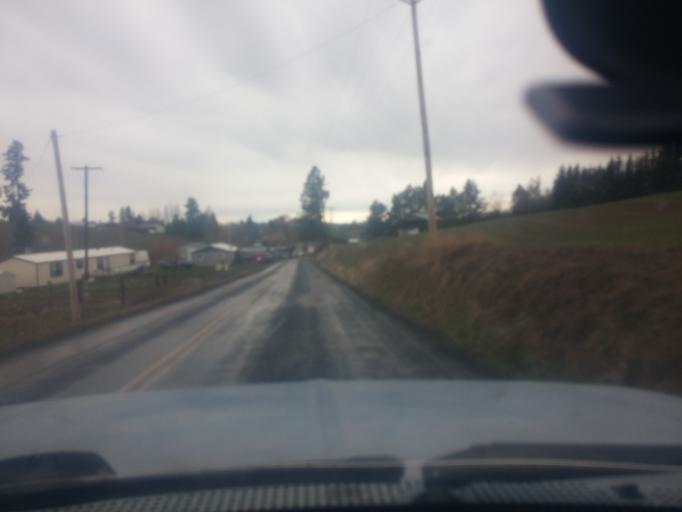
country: US
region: Idaho
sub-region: Latah County
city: Moscow
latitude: 46.9294
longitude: -116.8842
